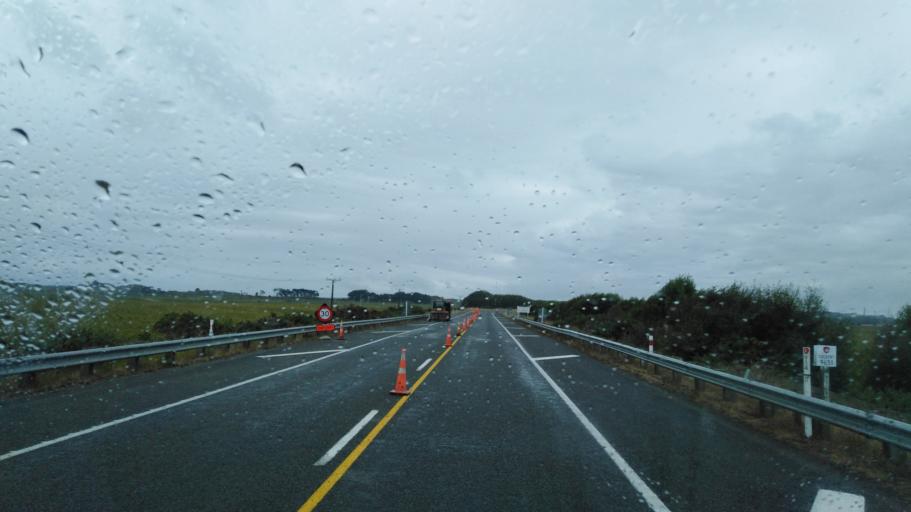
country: NZ
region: Manawatu-Wanganui
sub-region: Horowhenua District
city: Foxton
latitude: -40.5009
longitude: 175.2822
